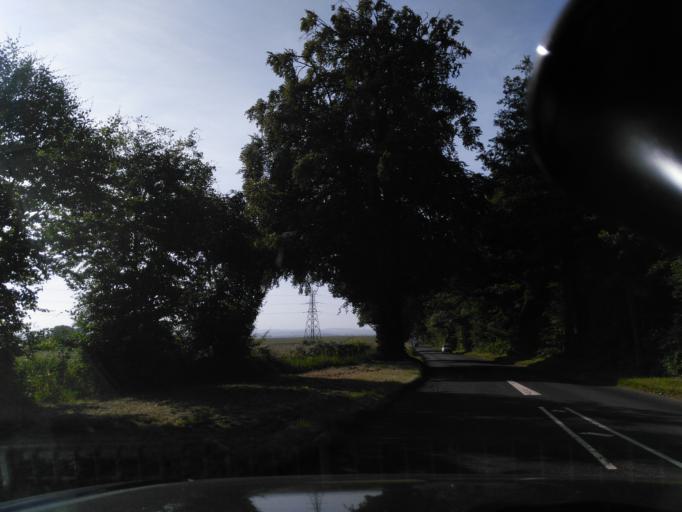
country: GB
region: England
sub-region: Wiltshire
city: Woodford
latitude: 51.1002
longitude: -1.8385
